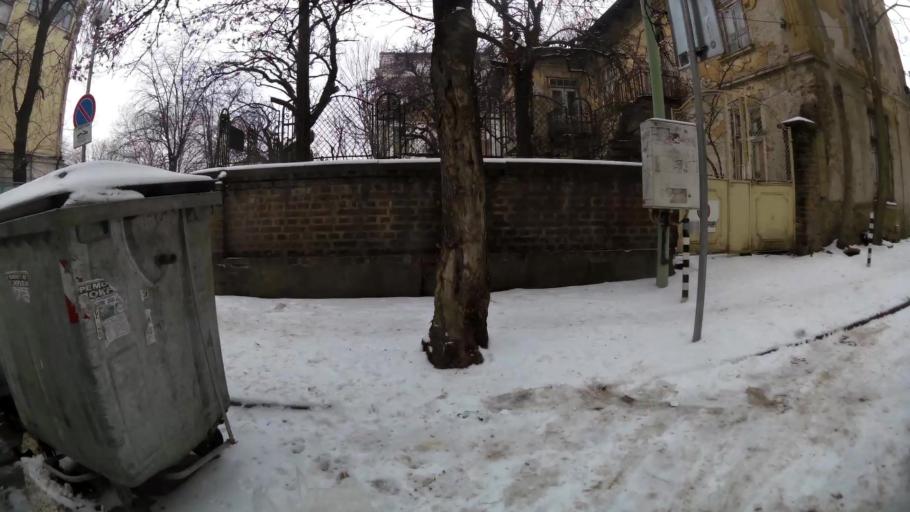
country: BG
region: Sofia-Capital
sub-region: Stolichna Obshtina
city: Sofia
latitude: 42.7067
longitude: 23.3185
